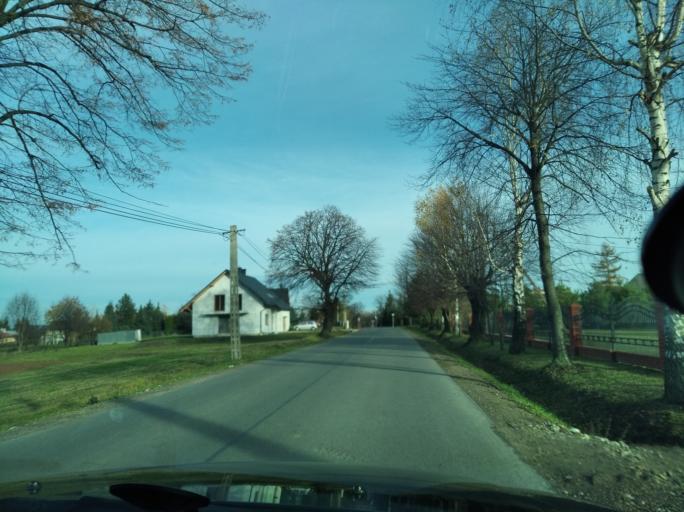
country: PL
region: Subcarpathian Voivodeship
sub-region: Powiat rzeszowski
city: Siedliska
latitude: 49.9501
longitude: 21.9820
